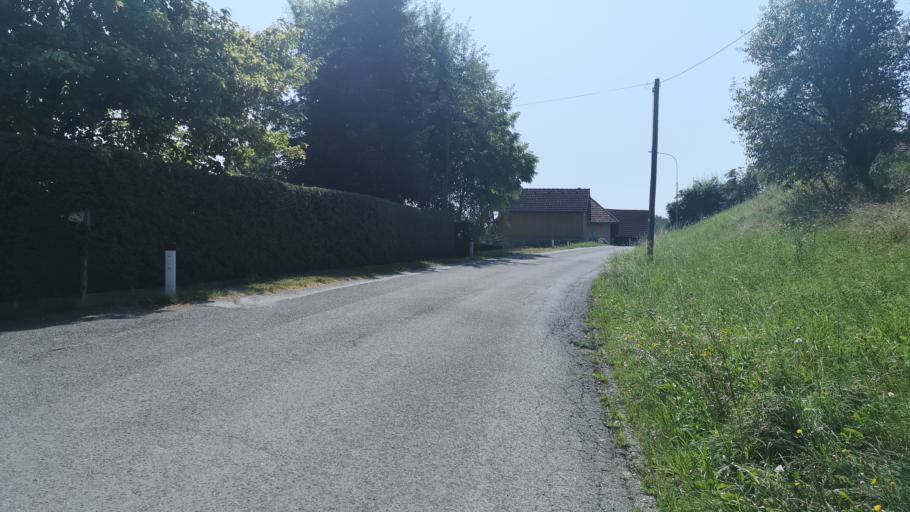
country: AT
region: Styria
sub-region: Politischer Bezirk Deutschlandsberg
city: Lannach
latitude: 46.9337
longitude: 15.3508
